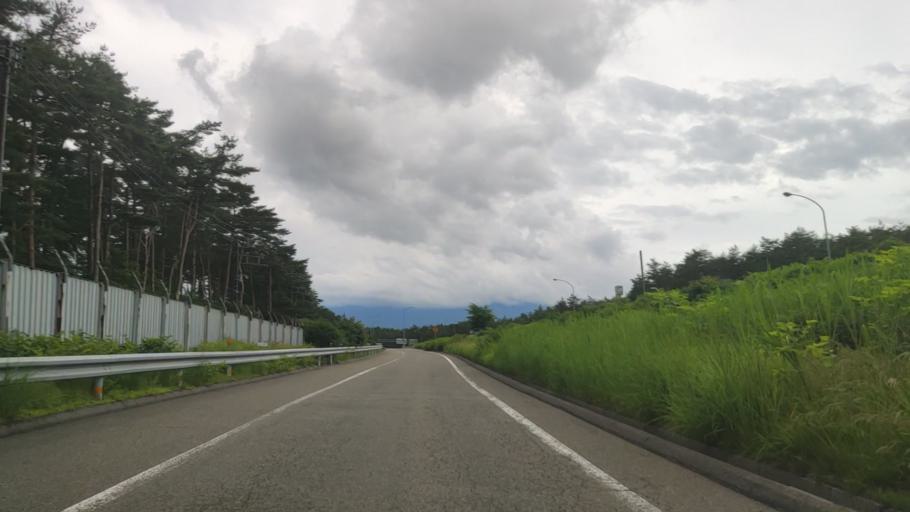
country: JP
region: Yamanashi
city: Fujikawaguchiko
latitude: 35.4799
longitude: 138.7723
